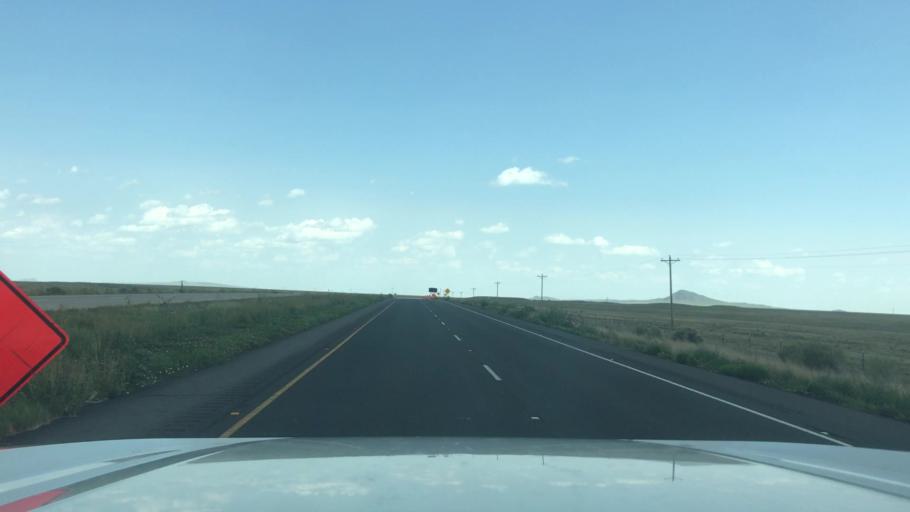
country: US
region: New Mexico
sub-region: Union County
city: Clayton
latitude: 36.6183
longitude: -103.6917
